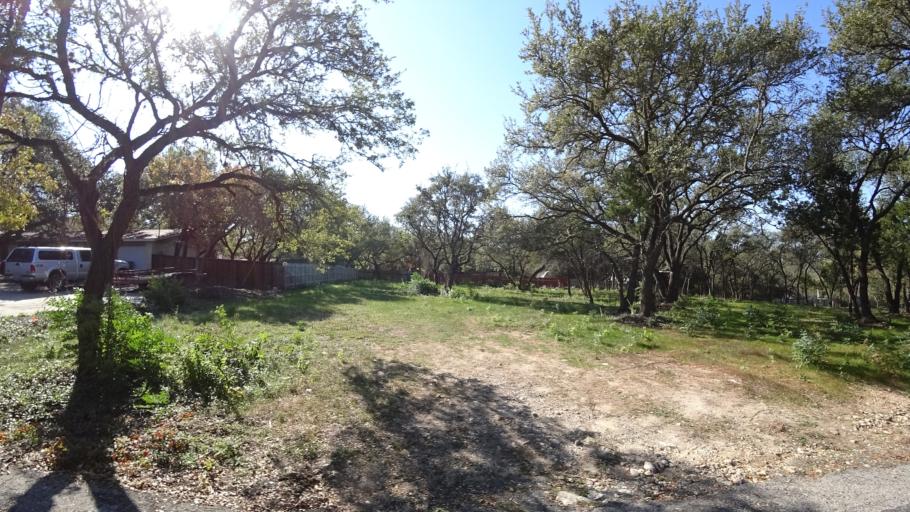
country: US
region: Texas
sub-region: Travis County
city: Barton Creek
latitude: 30.2314
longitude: -97.8733
